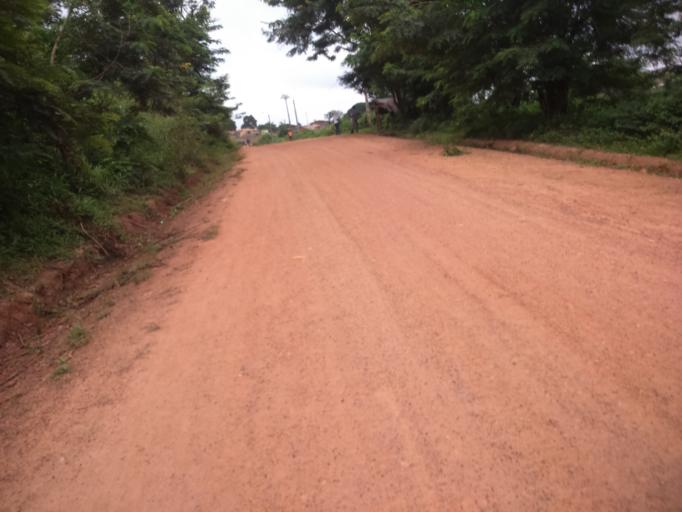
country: CI
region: Lagunes
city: Agou
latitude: 6.0894
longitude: -4.0644
